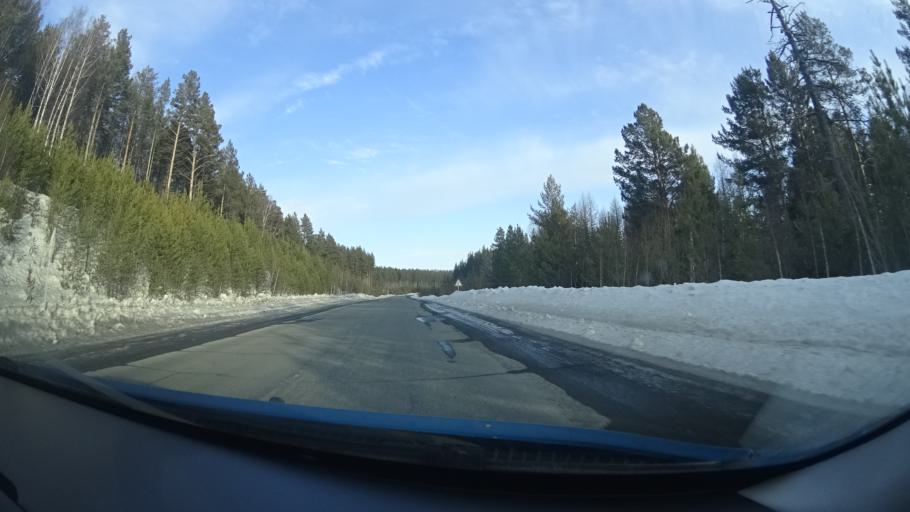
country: RU
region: Bashkortostan
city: Lomovka
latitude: 53.5272
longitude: 58.2486
